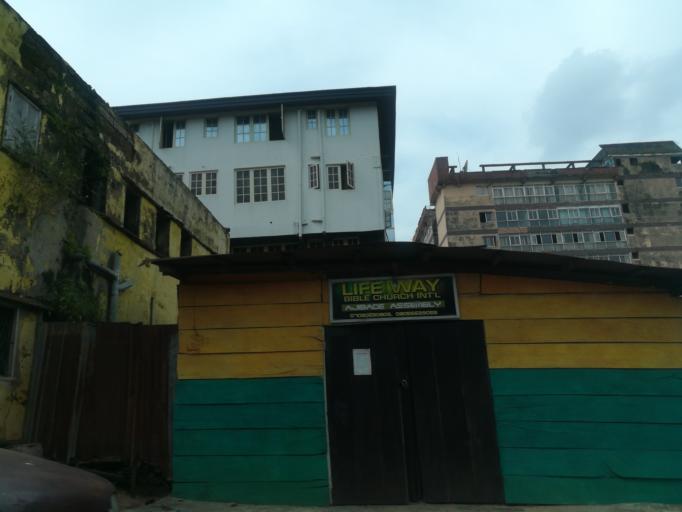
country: NG
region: Oyo
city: Ibadan
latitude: 7.4127
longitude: 3.8955
